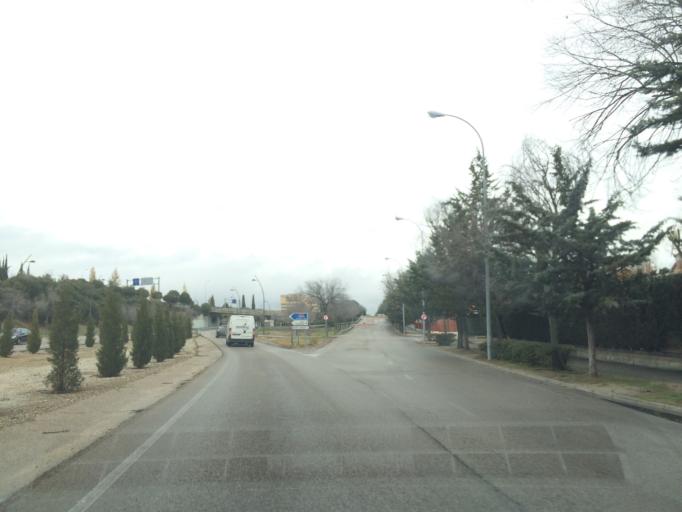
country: ES
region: Madrid
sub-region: Provincia de Madrid
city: Tres Cantos
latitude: 40.6070
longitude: -3.7190
